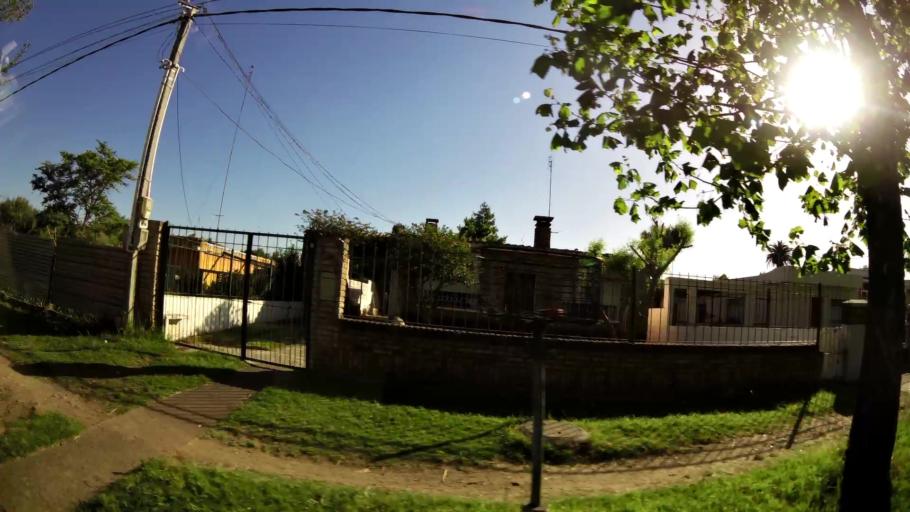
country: UY
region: Canelones
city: La Paz
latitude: -34.8143
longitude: -56.2224
